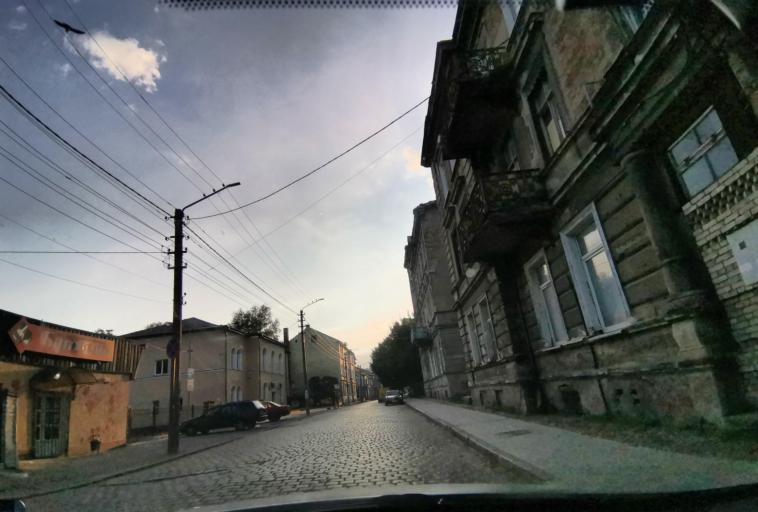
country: RU
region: Kaliningrad
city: Sovetsk
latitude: 55.0792
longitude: 21.9024
